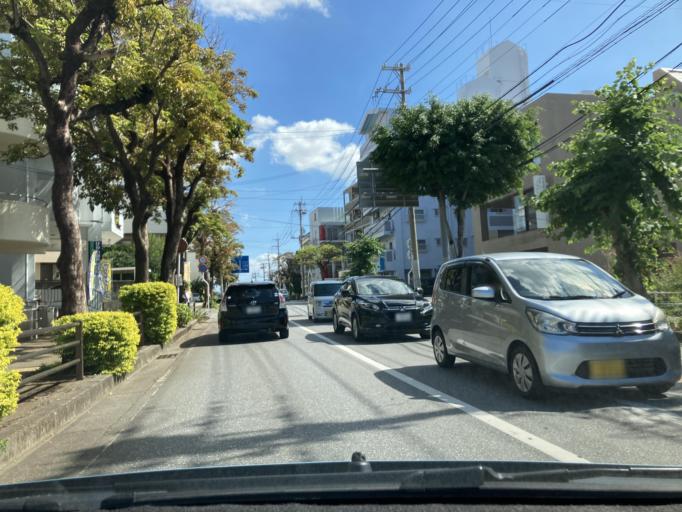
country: JP
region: Okinawa
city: Naha-shi
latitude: 26.2064
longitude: 127.6862
